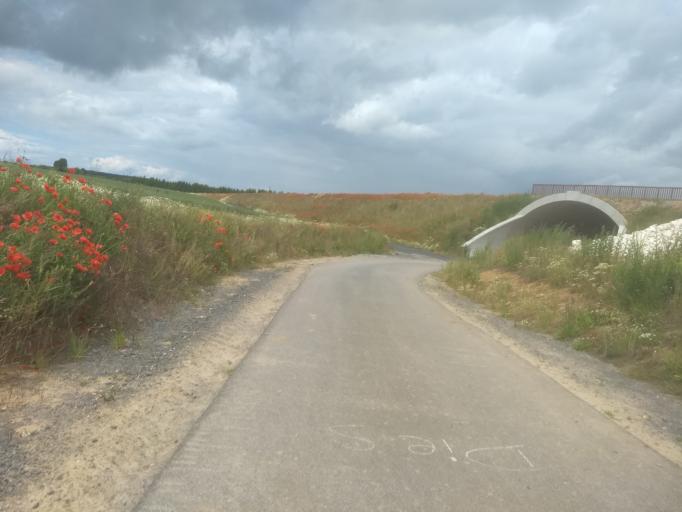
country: FR
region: Nord-Pas-de-Calais
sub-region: Departement du Pas-de-Calais
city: Dainville
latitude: 50.2650
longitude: 2.7128
